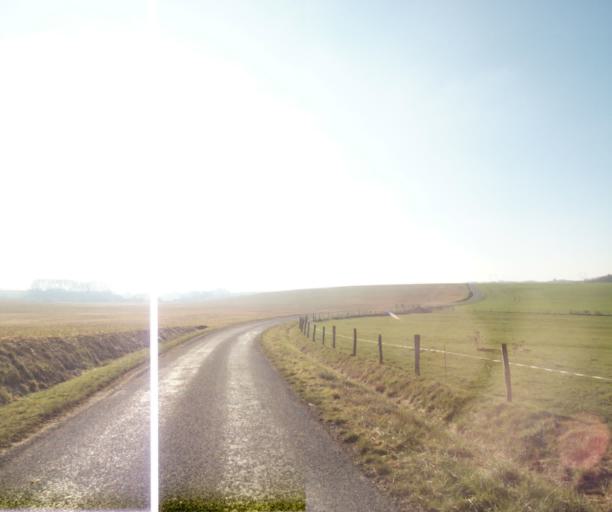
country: FR
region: Champagne-Ardenne
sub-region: Departement de la Haute-Marne
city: Wassy
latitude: 48.5217
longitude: 4.9903
